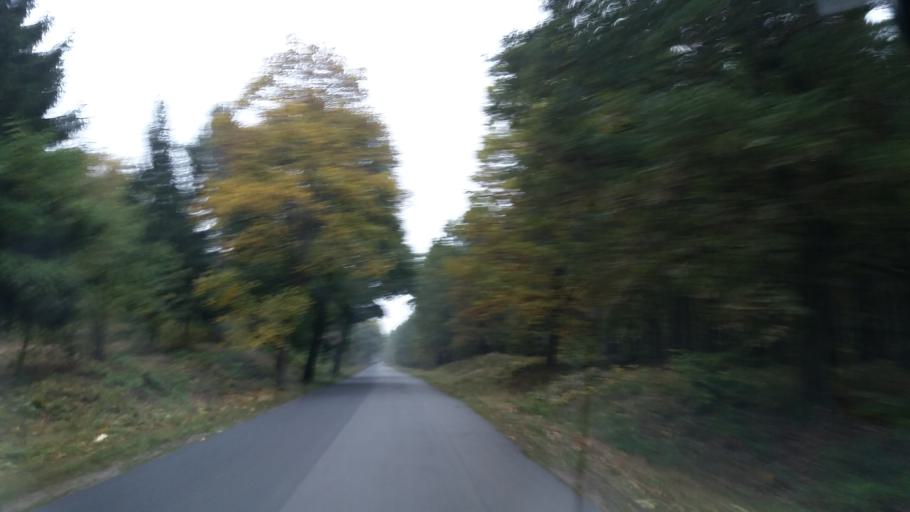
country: PL
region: Lubusz
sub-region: Powiat strzelecko-drezdenecki
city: Dobiegniew
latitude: 53.0579
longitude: 15.7597
